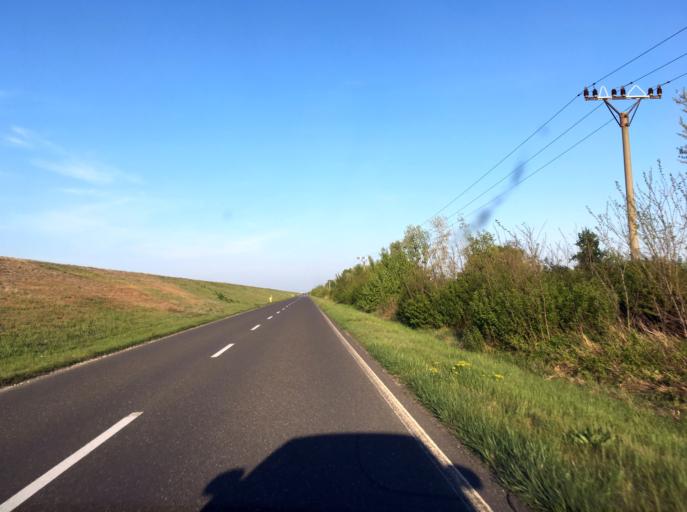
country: SK
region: Trnavsky
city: Samorin
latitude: 47.9966
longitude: 17.2820
